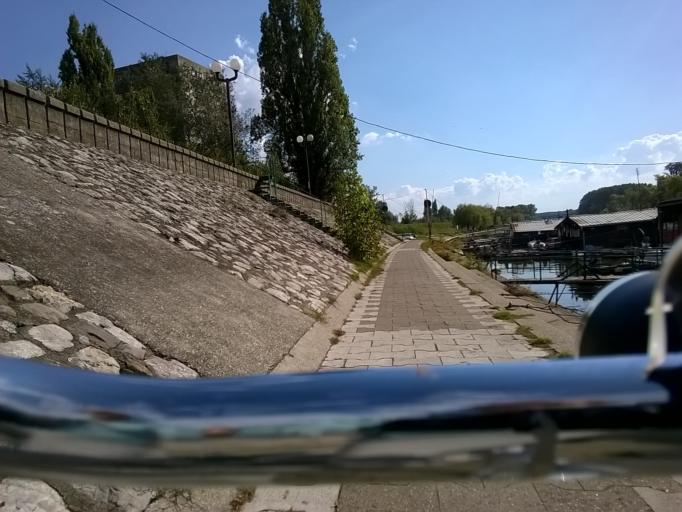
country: RS
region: Autonomna Pokrajina Vojvodina
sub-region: Juznobanatski Okrug
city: Pancevo
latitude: 44.8651
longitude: 20.6391
